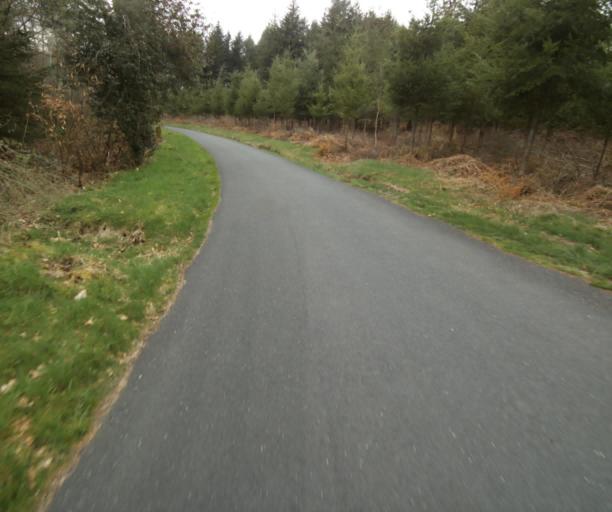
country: FR
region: Limousin
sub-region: Departement de la Correze
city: Correze
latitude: 45.3094
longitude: 1.9006
